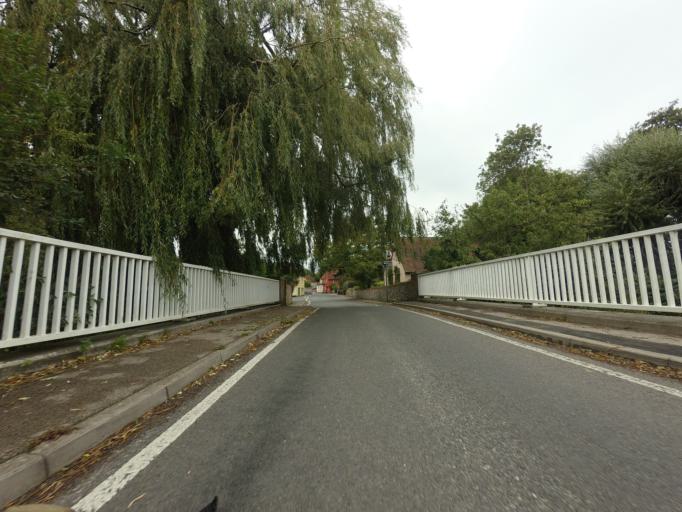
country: GB
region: England
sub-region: Essex
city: Saffron Walden
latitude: 52.0342
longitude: 0.2128
